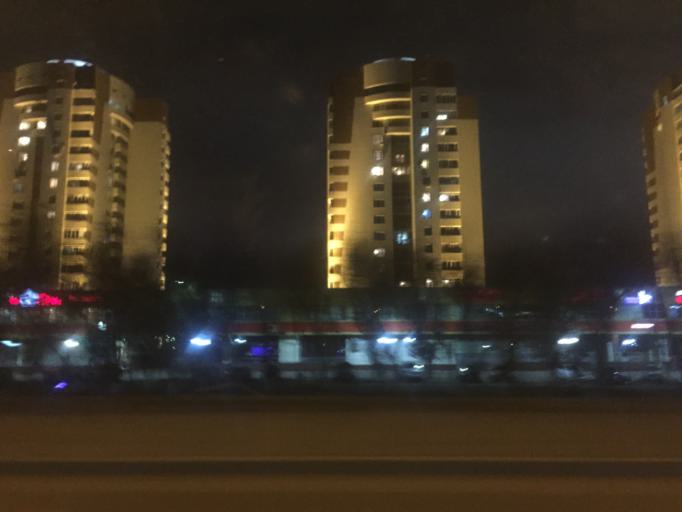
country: KZ
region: Astana Qalasy
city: Astana
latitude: 51.1496
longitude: 71.4251
